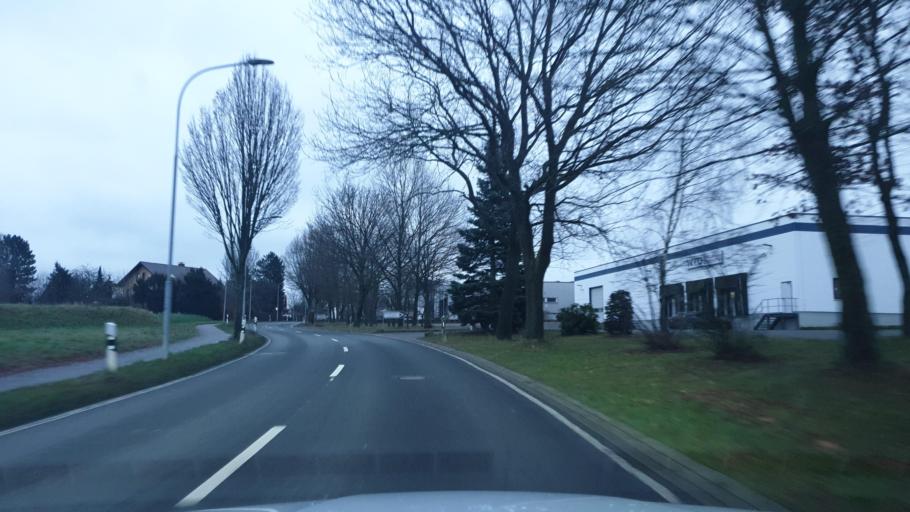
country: DE
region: North Rhine-Westphalia
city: Bad Oeynhausen
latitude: 52.1775
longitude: 8.8052
